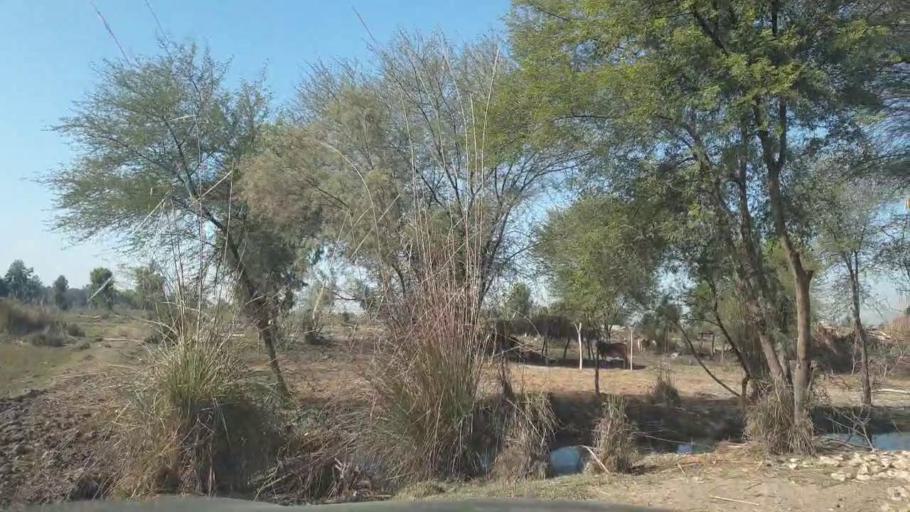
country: PK
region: Sindh
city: Mirpur Mathelo
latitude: 28.0601
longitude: 69.5101
